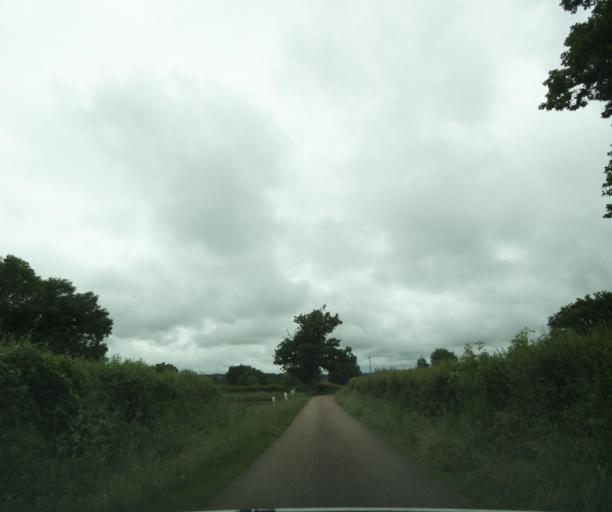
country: FR
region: Bourgogne
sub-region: Departement de Saone-et-Loire
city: Charolles
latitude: 46.4634
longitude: 4.3786
